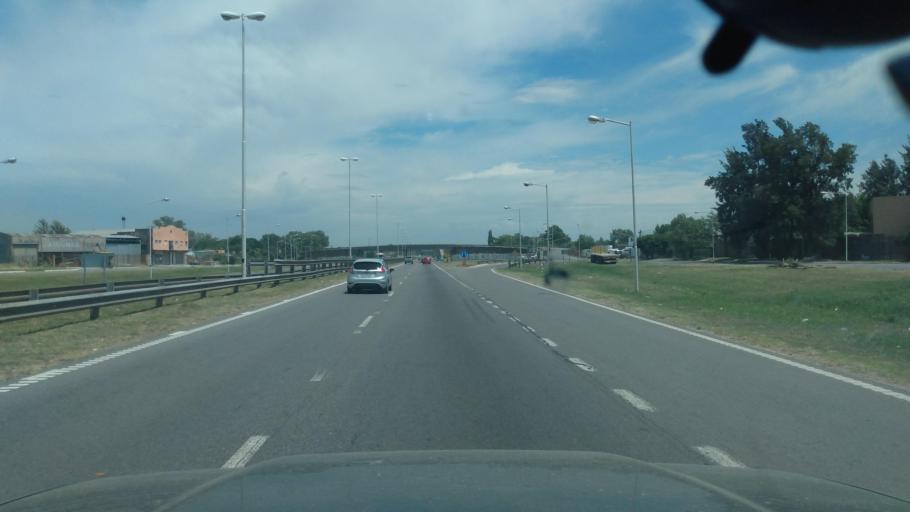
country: AR
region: Buenos Aires
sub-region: Partido de Lujan
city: Lujan
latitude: -34.5536
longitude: -59.1050
